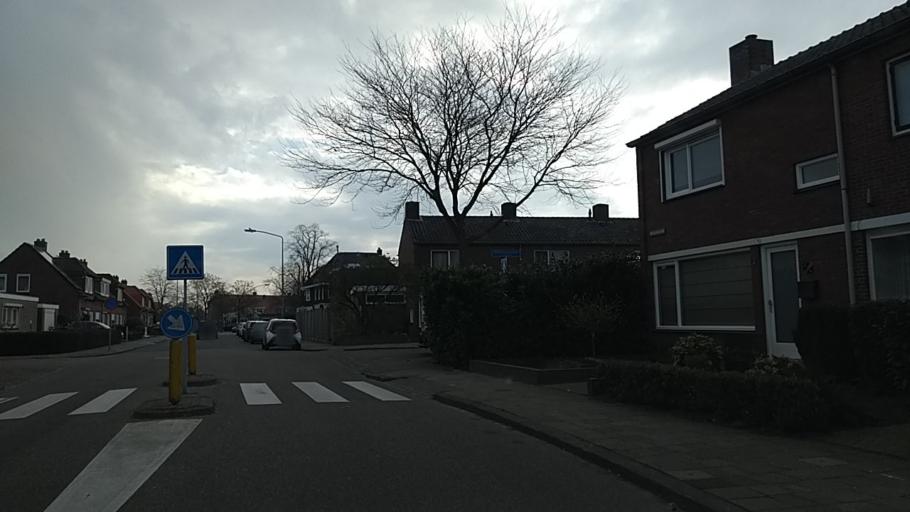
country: NL
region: Overijssel
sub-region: Gemeente Almelo
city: Almelo
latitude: 52.3474
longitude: 6.6470
